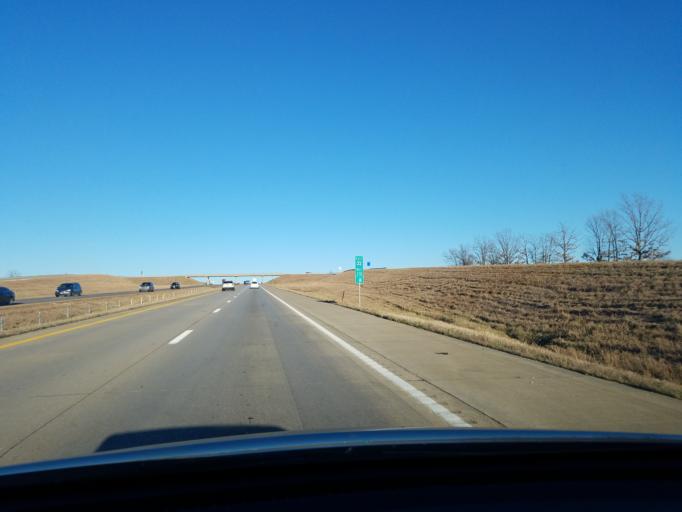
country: US
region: Missouri
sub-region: Crawford County
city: Cuba
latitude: 38.0917
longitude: -91.3719
